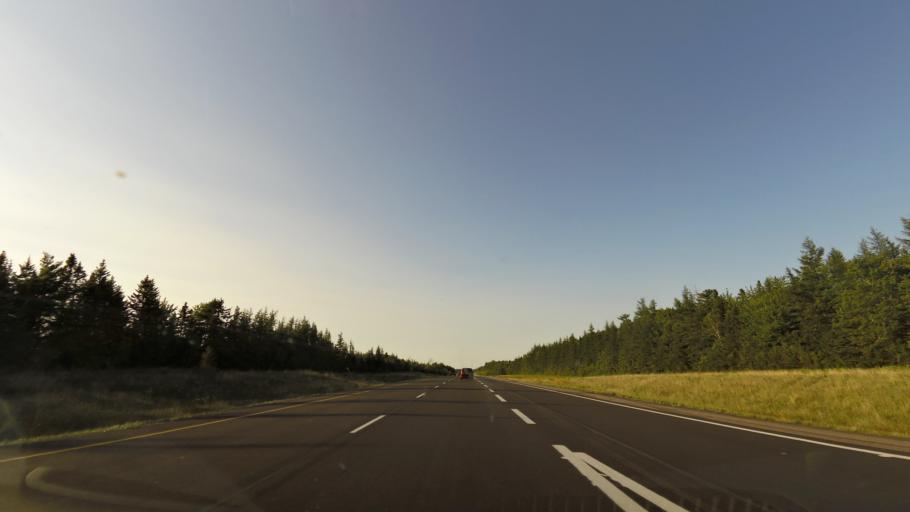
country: CA
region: New Brunswick
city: Dieppe
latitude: 46.0540
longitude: -64.5860
